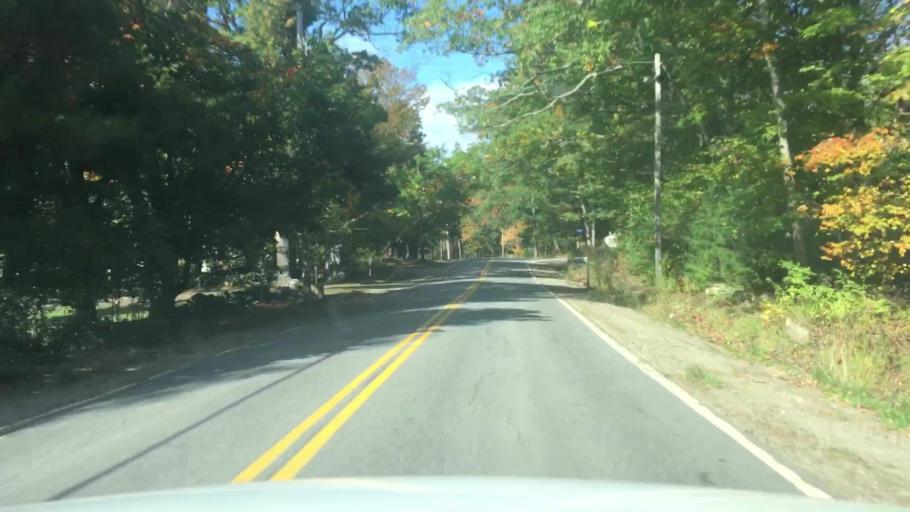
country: US
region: Maine
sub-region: Knox County
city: Warren
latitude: 44.1016
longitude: -69.2214
